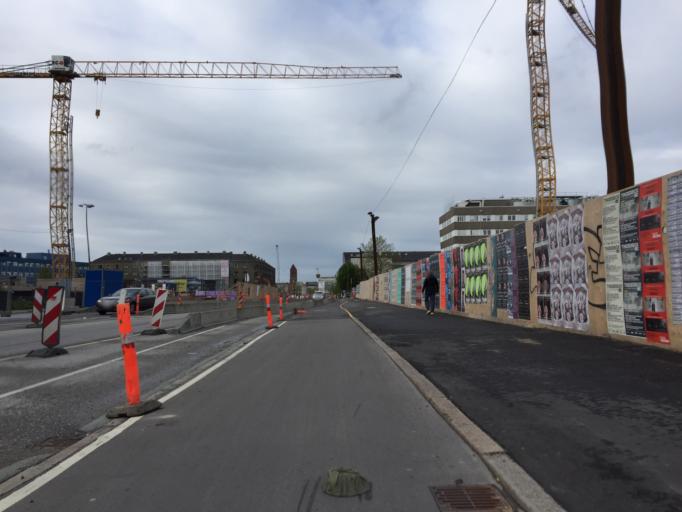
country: DK
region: Capital Region
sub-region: Kobenhavn
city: Copenhagen
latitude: 55.7004
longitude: 12.5560
